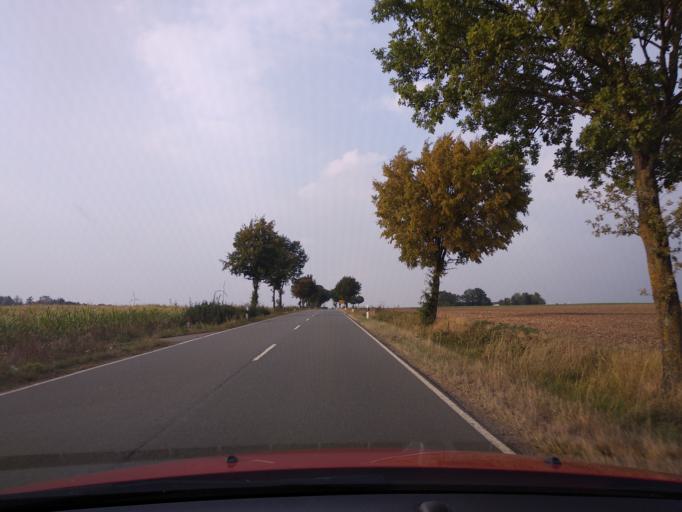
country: DE
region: North Rhine-Westphalia
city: Borgentreich
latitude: 51.5563
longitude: 9.2978
